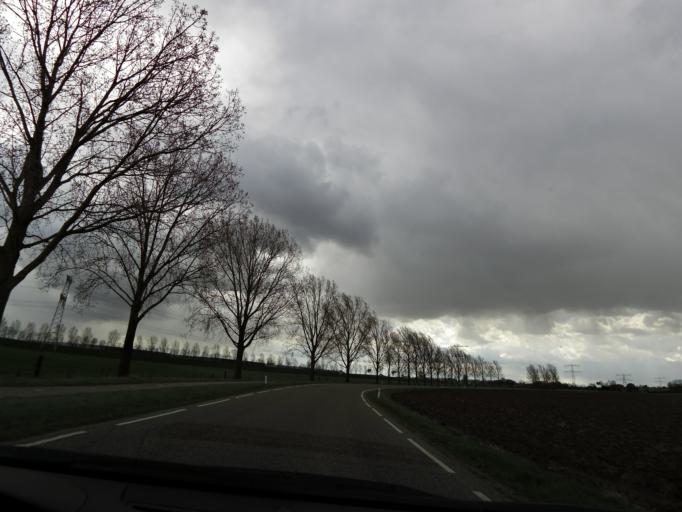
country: NL
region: Limburg
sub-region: Gemeente Sittard-Geleen
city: Born
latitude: 51.0688
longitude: 5.8095
